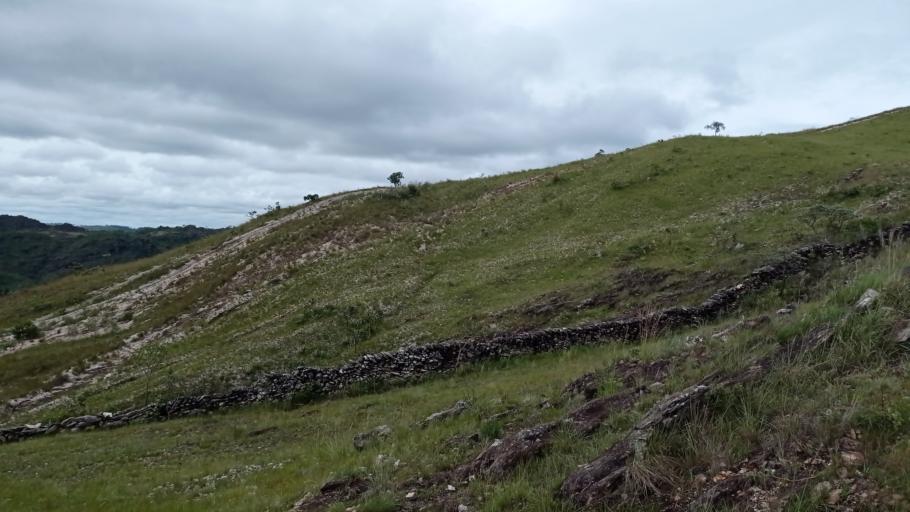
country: BR
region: Minas Gerais
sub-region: Sao Joao Del Rei
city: Sao Joao del Rei
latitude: -21.1173
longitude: -44.2803
